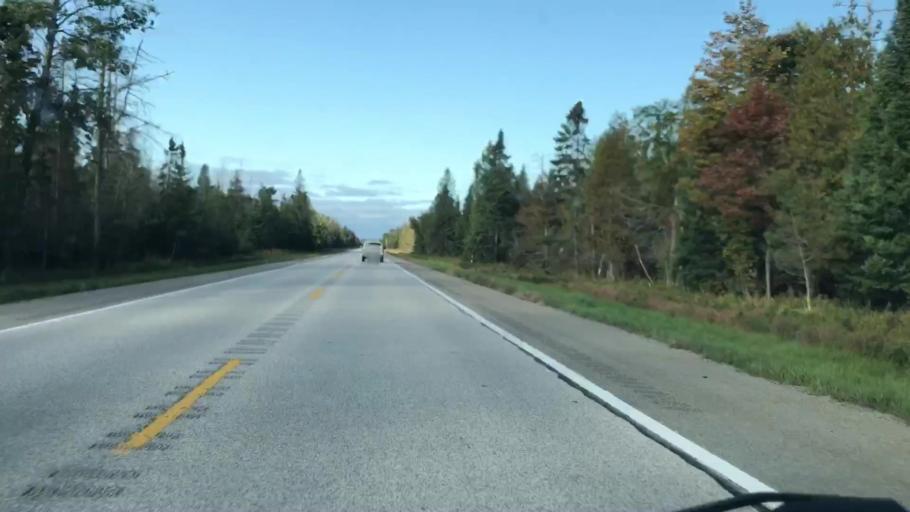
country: US
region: Michigan
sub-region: Luce County
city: Newberry
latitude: 46.3264
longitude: -85.1657
